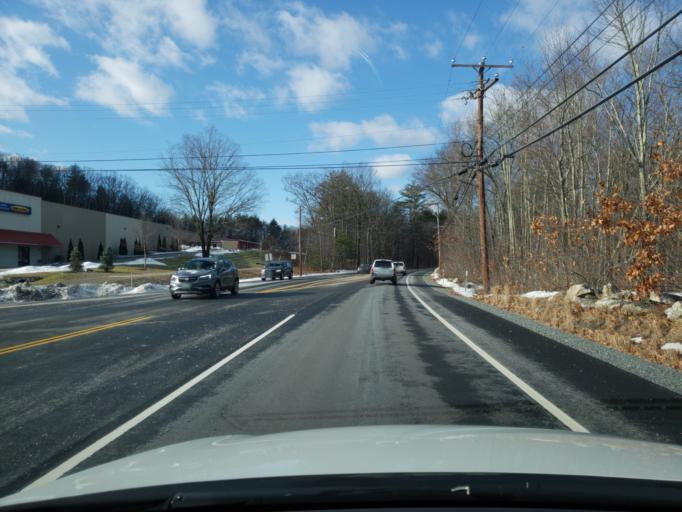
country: US
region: New Hampshire
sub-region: Hillsborough County
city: Goffstown
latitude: 43.0149
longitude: -71.5629
